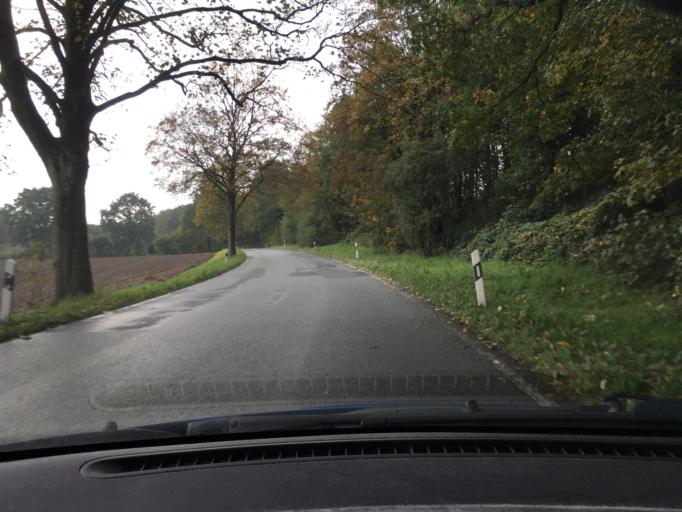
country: DE
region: Schleswig-Holstein
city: Tensfeld
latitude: 54.0368
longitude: 10.3129
